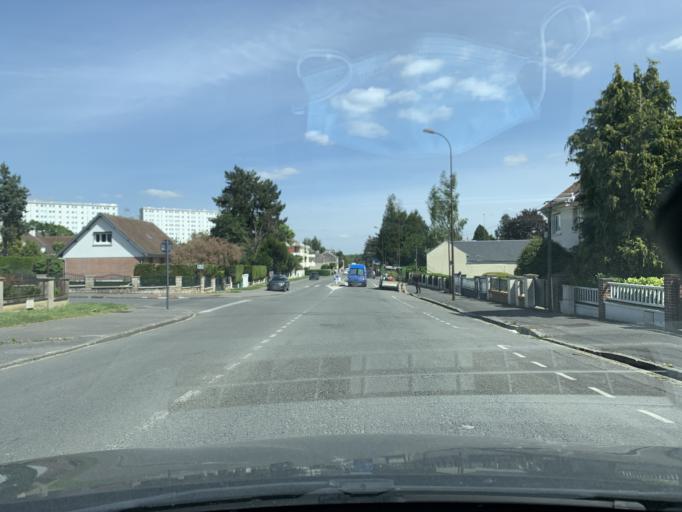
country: FR
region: Picardie
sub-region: Departement de l'Aisne
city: Saint-Quentin
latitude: 49.8583
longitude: 3.2985
